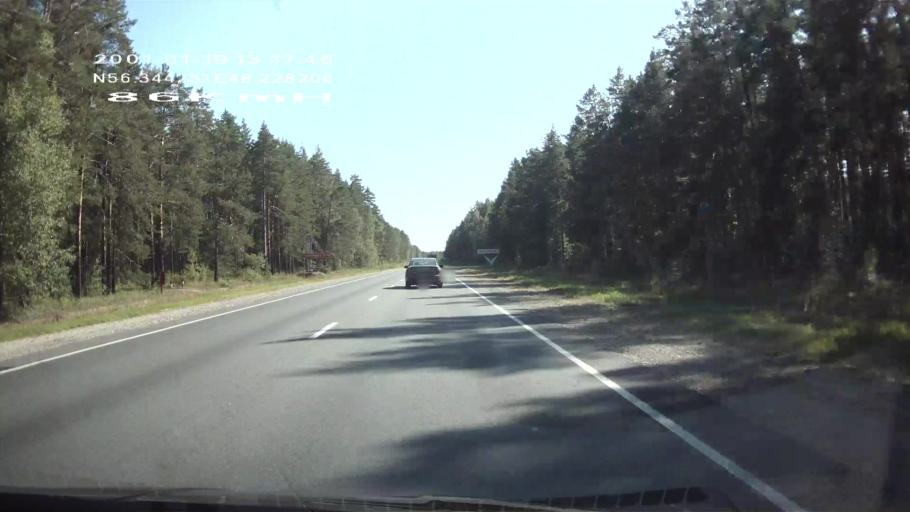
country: RU
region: Mariy-El
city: Suslonger
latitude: 56.3439
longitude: 48.2284
